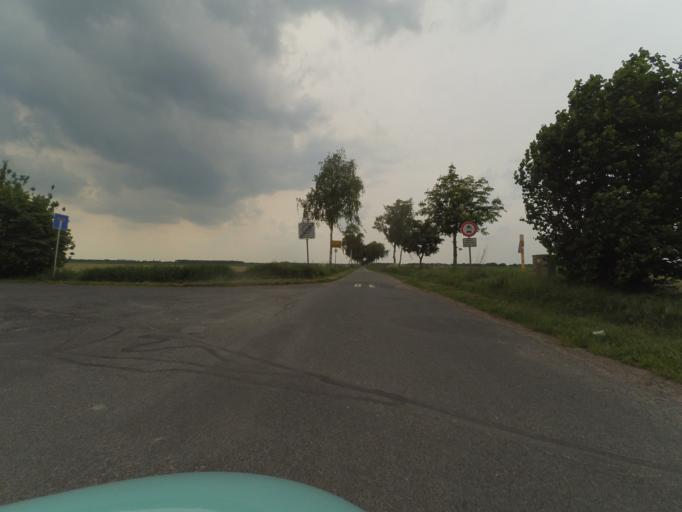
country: DE
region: Lower Saxony
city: Arpke
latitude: 52.3965
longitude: 10.0500
